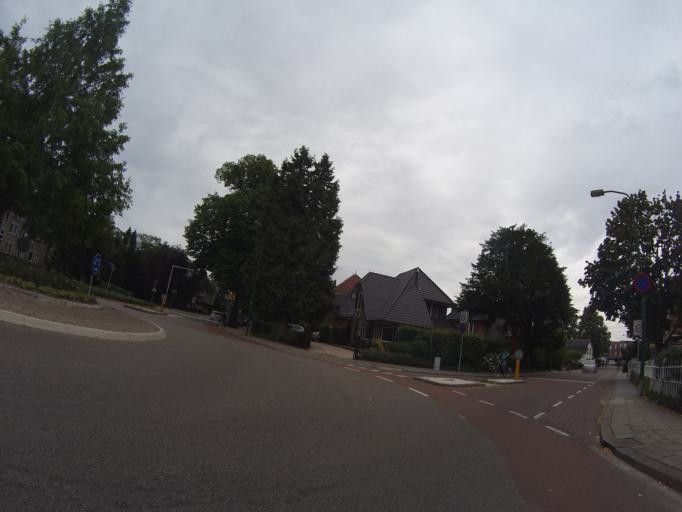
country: NL
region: Utrecht
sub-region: Gemeente Baarn
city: Baarn
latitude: 52.2146
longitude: 5.2822
